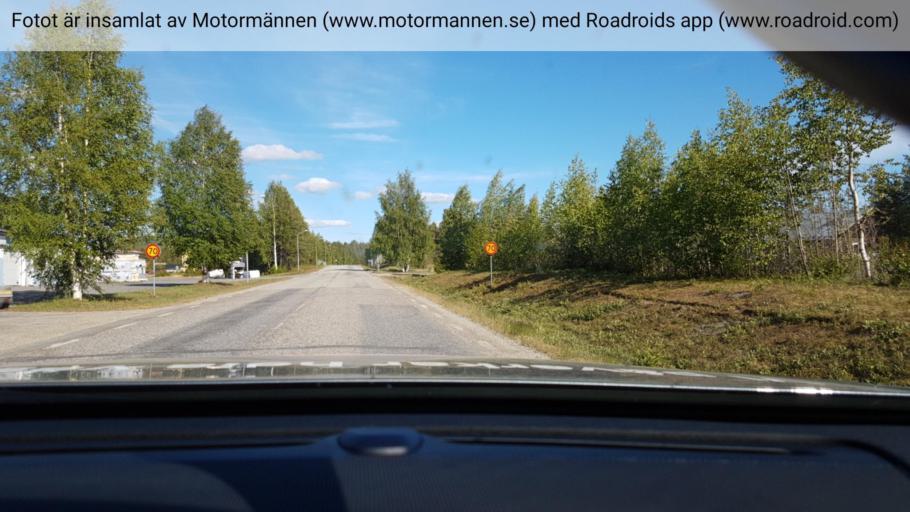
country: SE
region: Vaesterbotten
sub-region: Lycksele Kommun
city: Lycksele
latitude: 64.8132
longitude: 18.9068
